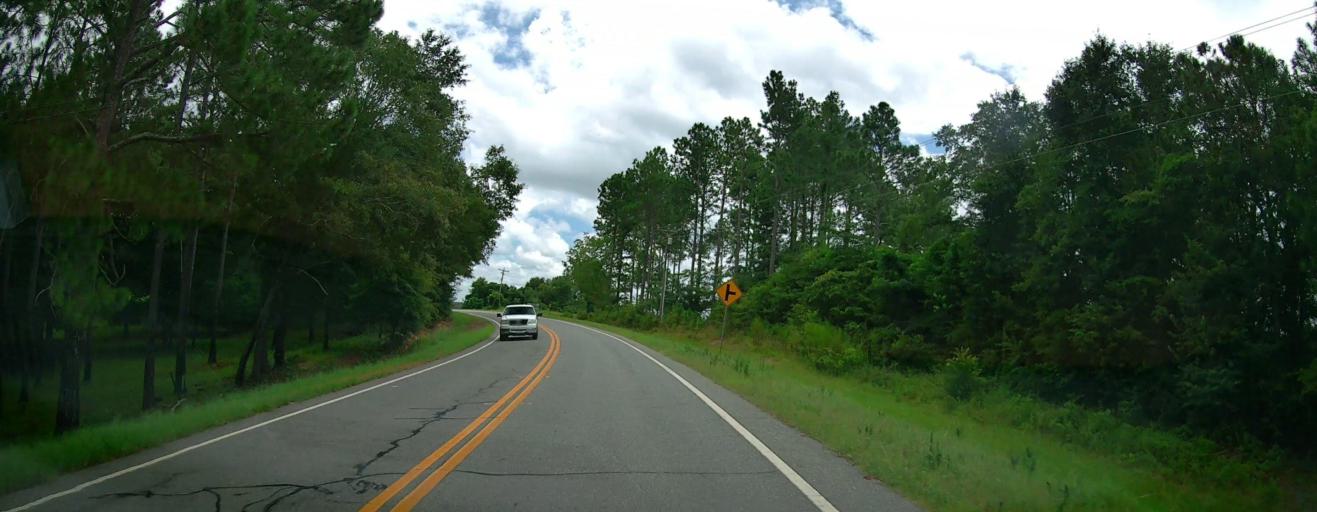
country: US
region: Georgia
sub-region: Wilcox County
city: Rochelle
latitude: 32.0248
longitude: -83.5654
